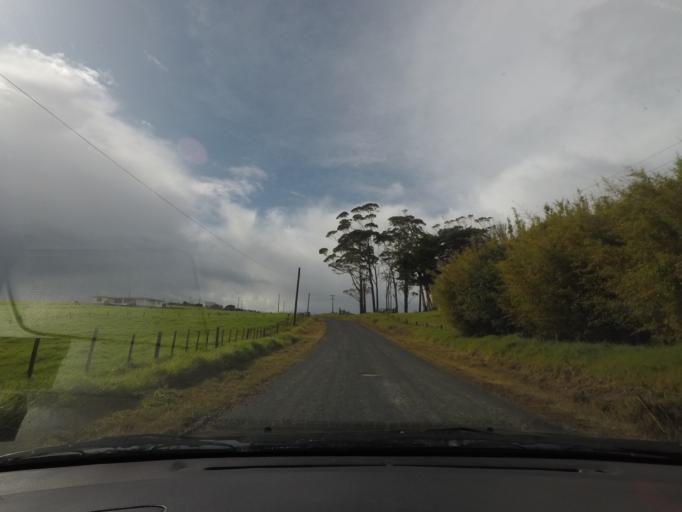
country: NZ
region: Auckland
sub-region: Auckland
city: Warkworth
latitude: -36.4317
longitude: 174.7199
